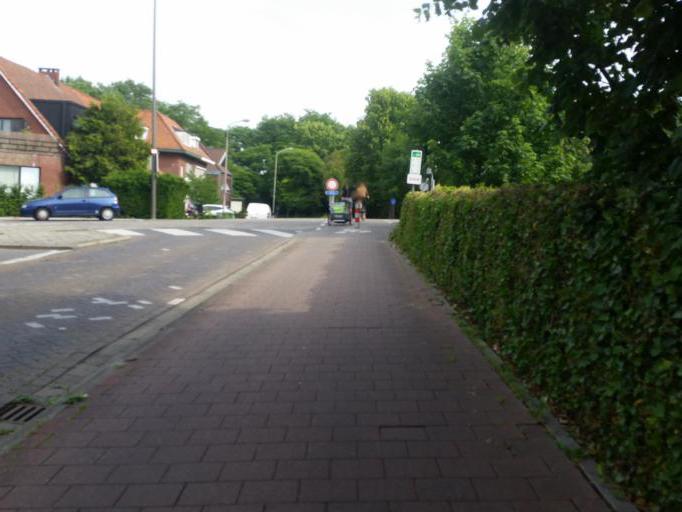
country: BE
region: Flanders
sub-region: Provincie Antwerpen
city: Mortsel
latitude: 51.1766
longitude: 4.4523
